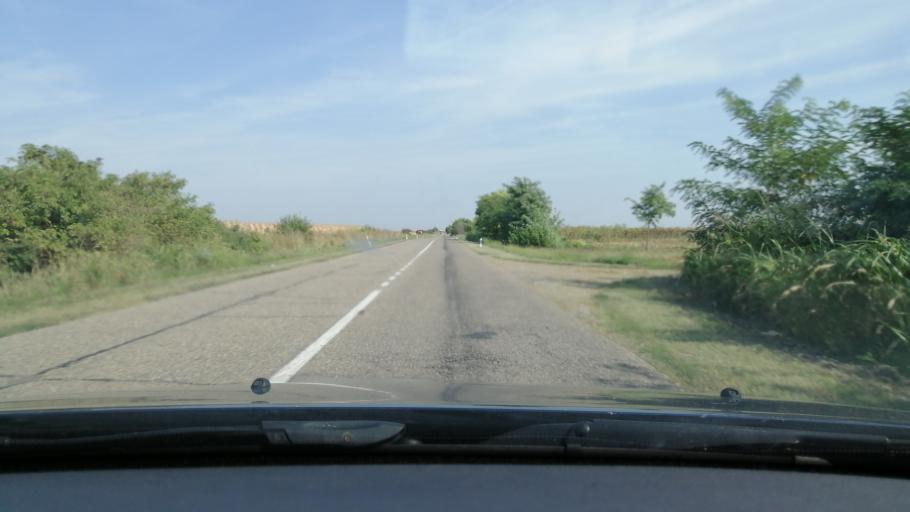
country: RS
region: Autonomna Pokrajina Vojvodina
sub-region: Juznobanatski Okrug
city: Kovacica
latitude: 45.1422
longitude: 20.6164
